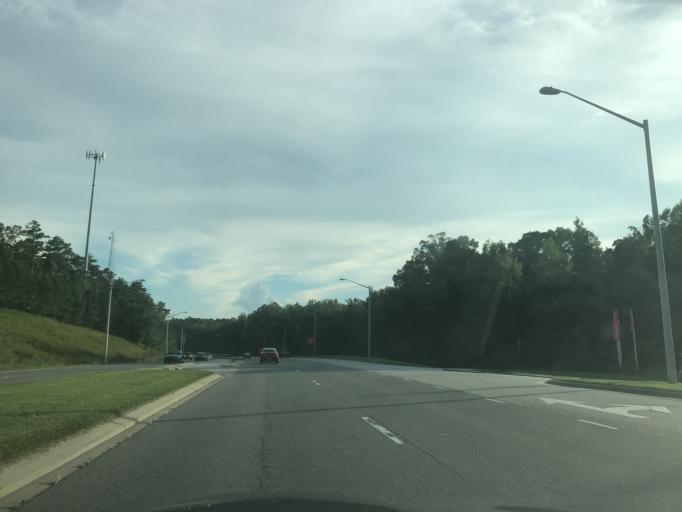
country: US
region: North Carolina
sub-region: Wake County
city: Green Level
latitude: 35.8578
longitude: -78.8945
